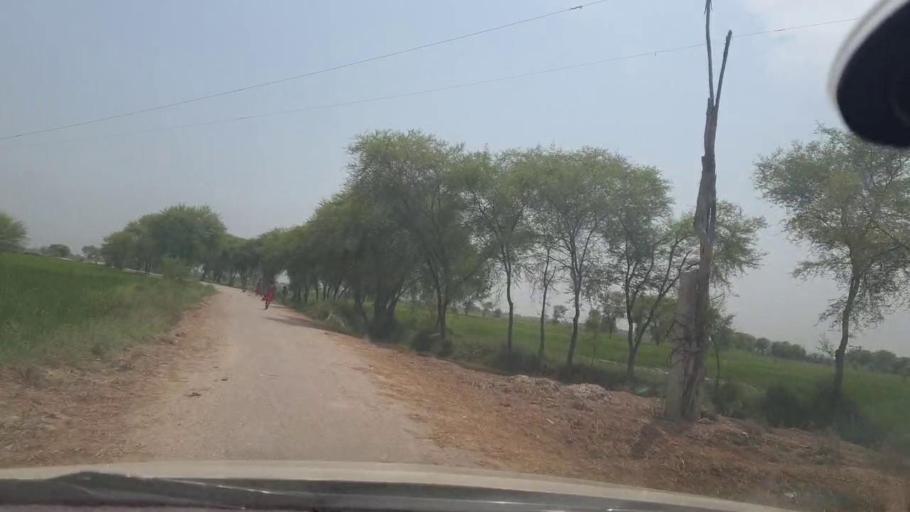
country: PK
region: Sindh
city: Jacobabad
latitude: 28.1741
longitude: 68.3869
